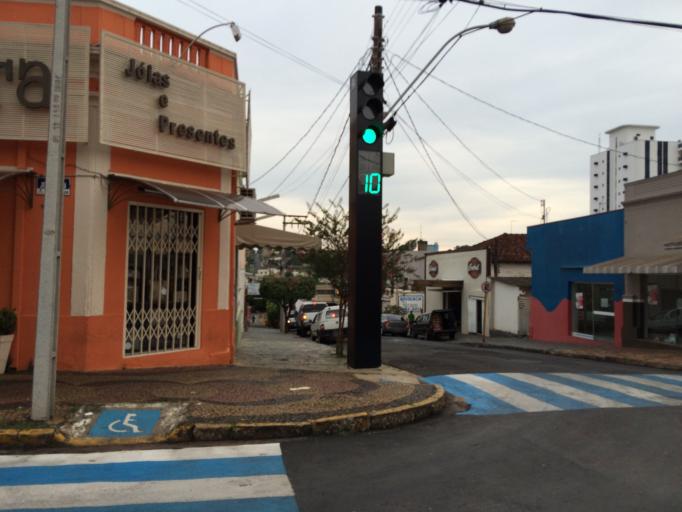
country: BR
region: Sao Paulo
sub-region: Matao
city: Matao
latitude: -21.6026
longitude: -48.3639
